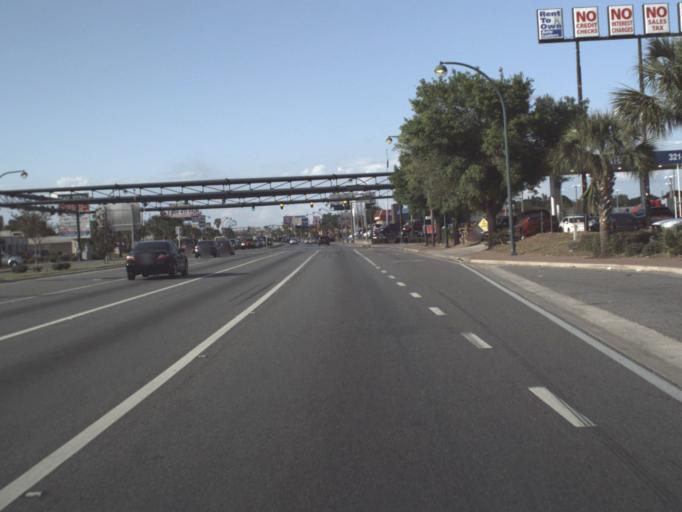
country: US
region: Florida
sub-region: Orange County
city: Sky Lake
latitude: 28.4642
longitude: -81.3969
